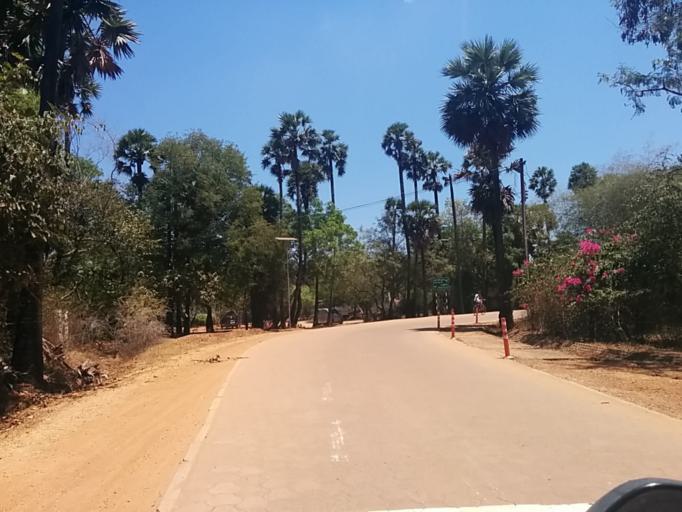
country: IN
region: Tamil Nadu
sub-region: Villupuram
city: Auroville
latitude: 12.0059
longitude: 79.8024
